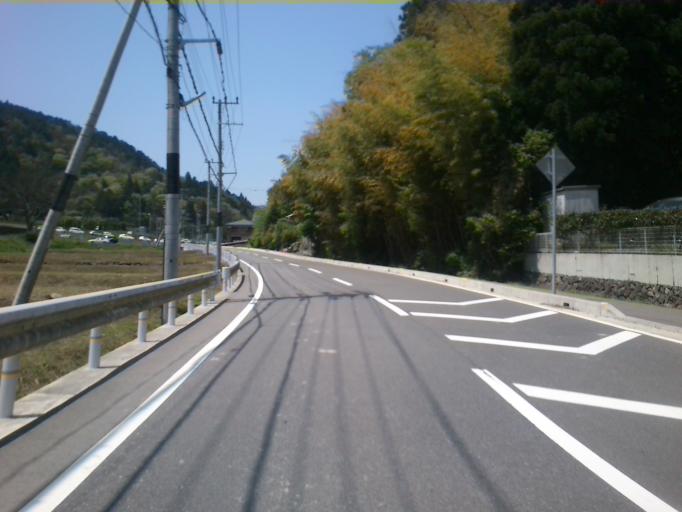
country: JP
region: Kyoto
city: Kameoka
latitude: 34.9501
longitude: 135.5436
